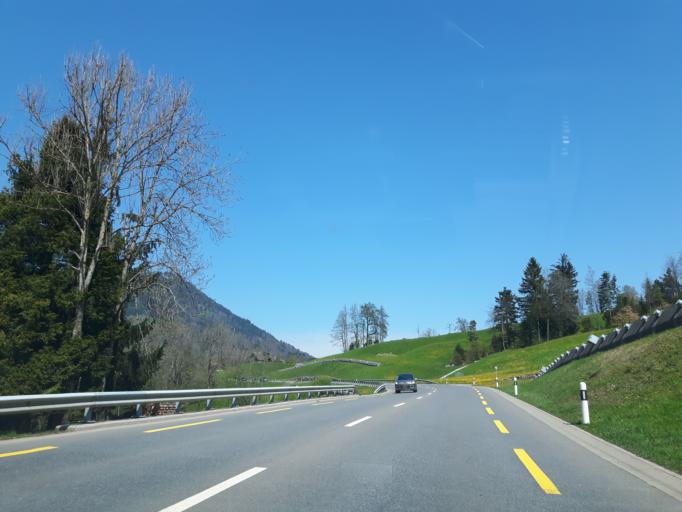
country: CH
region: Schwyz
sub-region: Bezirk Schwyz
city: Sattel
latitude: 47.0666
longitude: 8.6235
